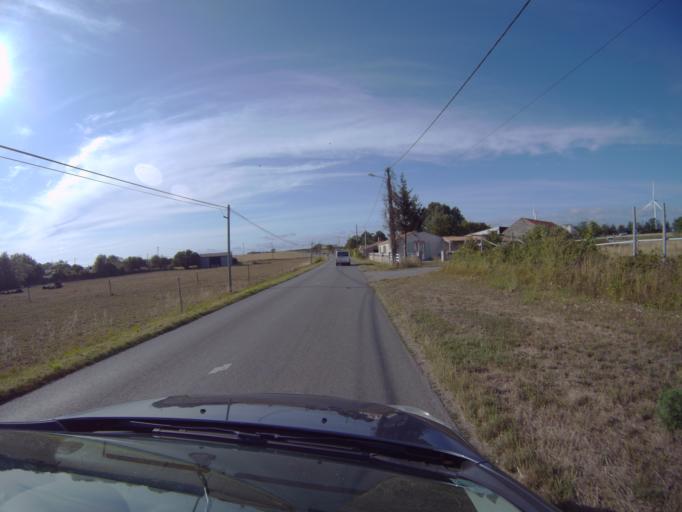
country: FR
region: Pays de la Loire
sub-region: Departement de la Vendee
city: Longeville-sur-Mer
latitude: 46.4138
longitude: -1.4537
